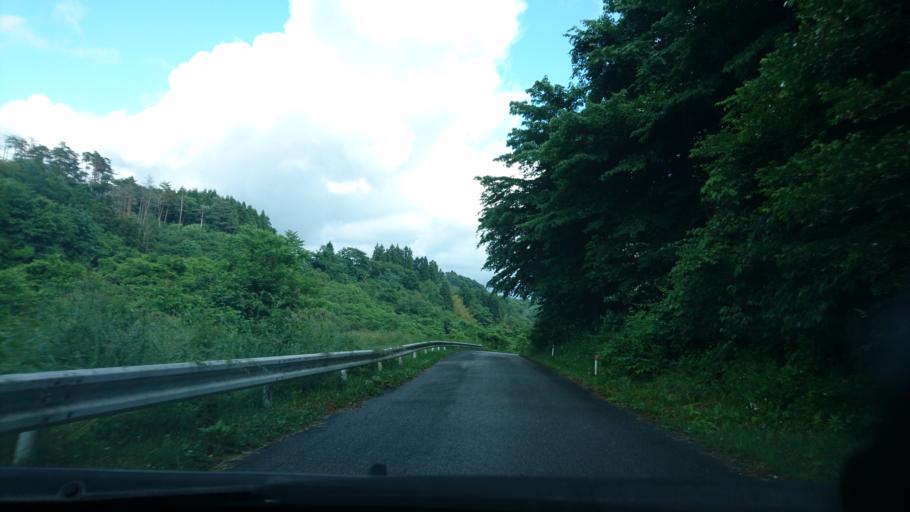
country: JP
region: Iwate
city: Ichinoseki
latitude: 38.8691
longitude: 141.2825
